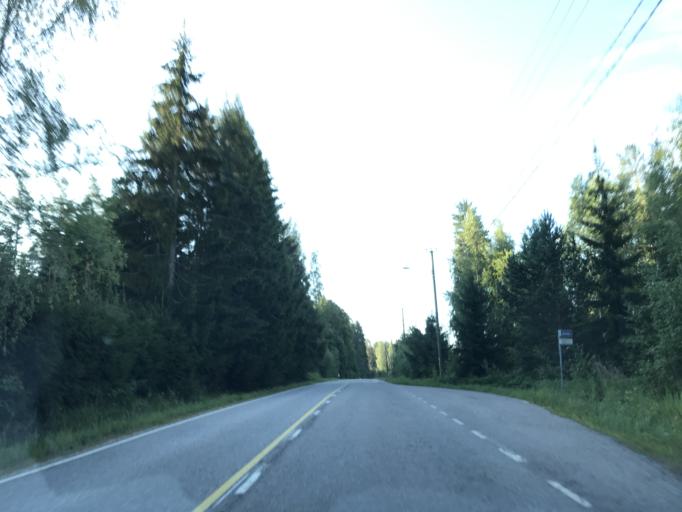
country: FI
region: Uusimaa
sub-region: Helsinki
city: Nurmijaervi
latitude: 60.3782
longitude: 24.6749
